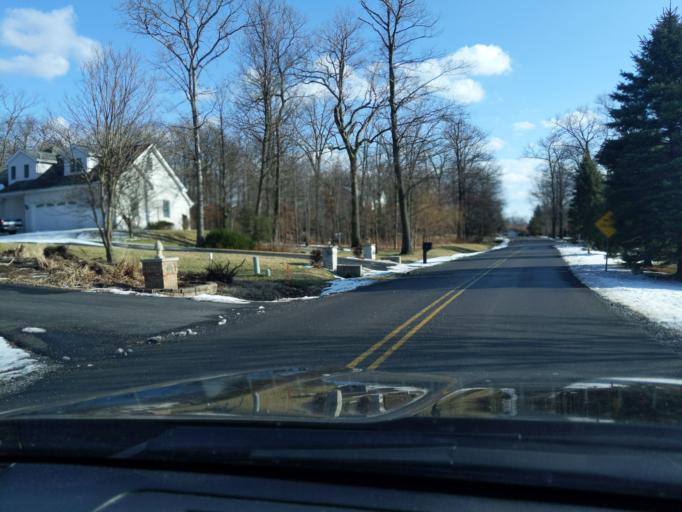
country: US
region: Pennsylvania
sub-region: Blair County
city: Lakemont
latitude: 40.4713
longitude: -78.3733
